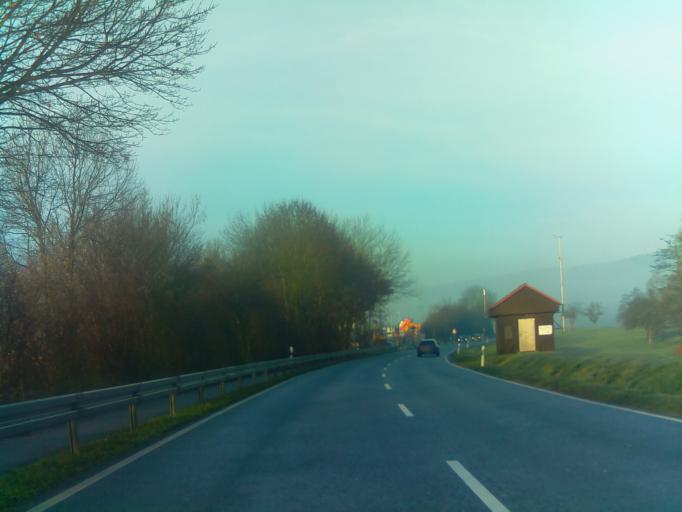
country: DE
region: Hesse
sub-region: Regierungsbezirk Darmstadt
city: Rimbach
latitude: 49.6416
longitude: 8.7582
